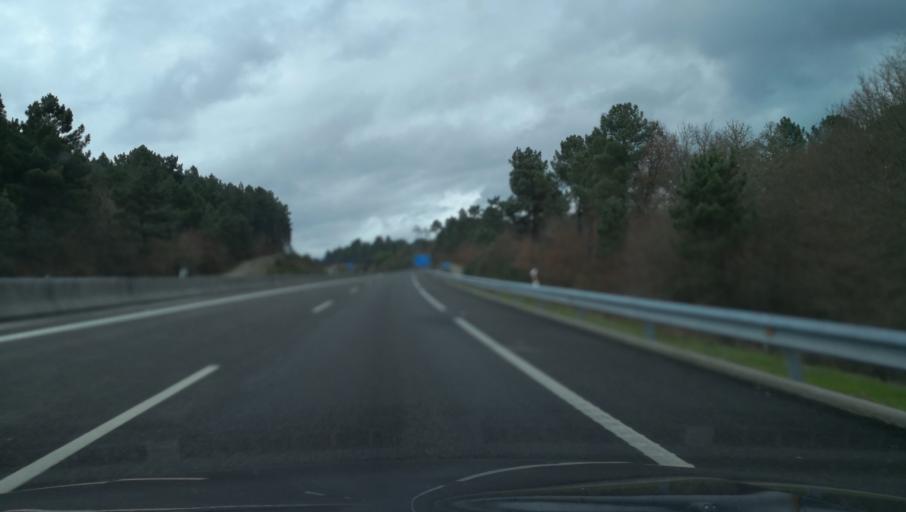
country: ES
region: Galicia
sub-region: Provincia de Ourense
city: Maside
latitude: 42.4378
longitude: -8.0183
